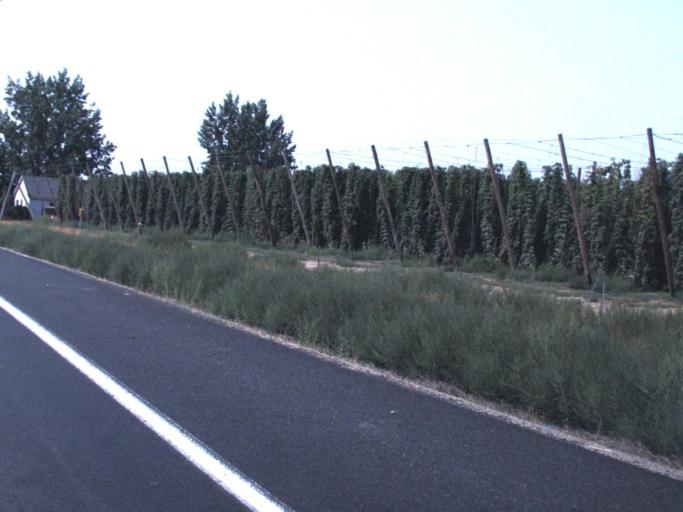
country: US
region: Washington
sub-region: Yakima County
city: Terrace Heights
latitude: 46.5496
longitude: -120.3387
